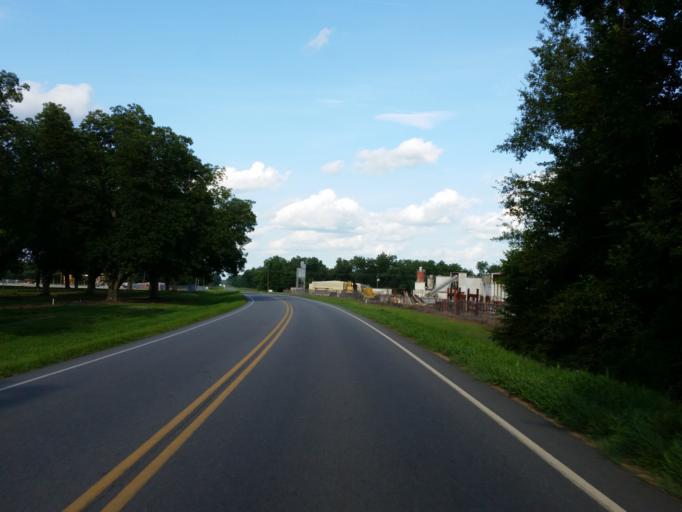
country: US
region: Georgia
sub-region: Crisp County
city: Cordele
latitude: 31.9576
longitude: -83.9790
